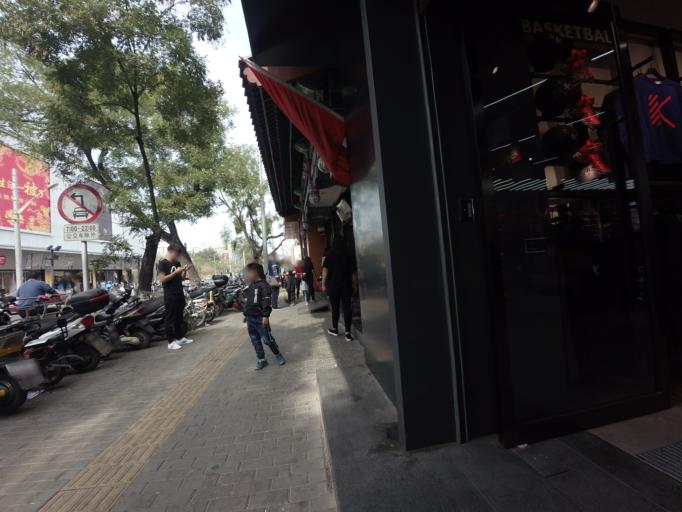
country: CN
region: Beijing
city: Jinrongjie
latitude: 39.9387
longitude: 116.3669
